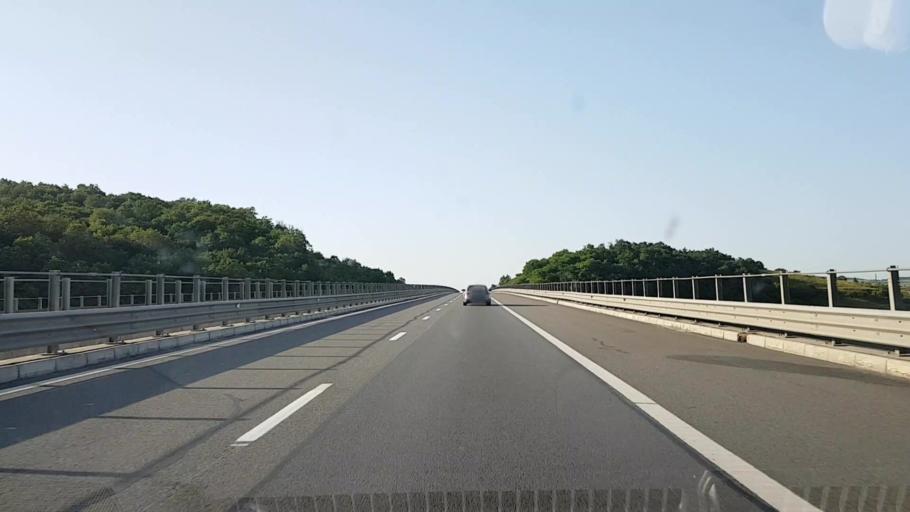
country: RO
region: Cluj
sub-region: Comuna Floresti
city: Luna de Sus
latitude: 46.7343
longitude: 23.4191
